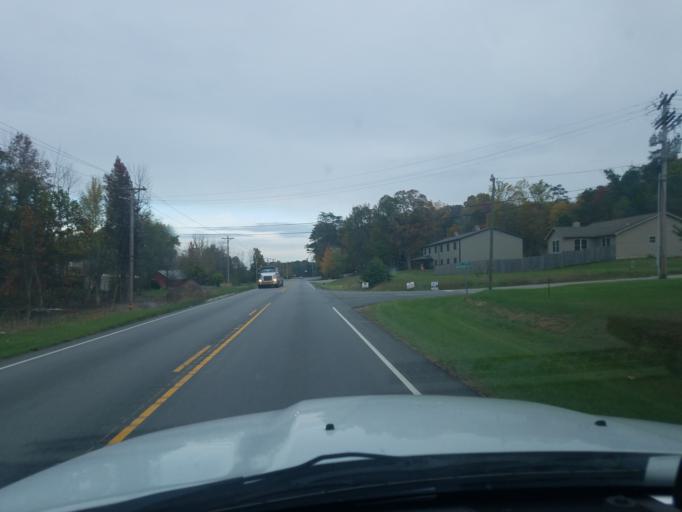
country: US
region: Indiana
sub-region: Floyd County
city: Galena
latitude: 38.4437
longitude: -85.8670
